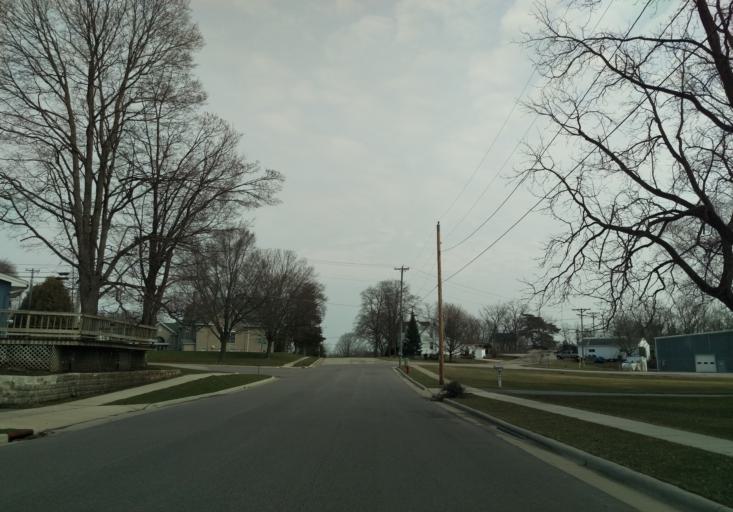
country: US
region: Wisconsin
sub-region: Columbia County
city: Lodi
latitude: 43.3102
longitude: -89.5317
